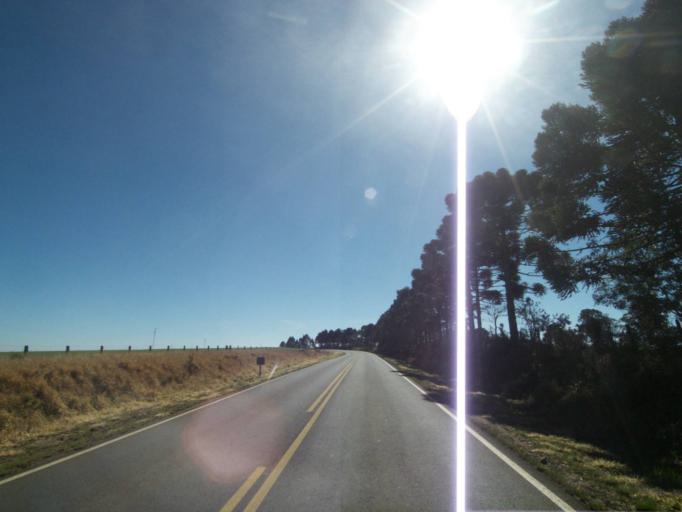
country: BR
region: Parana
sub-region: Castro
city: Castro
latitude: -24.6739
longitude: -50.2137
